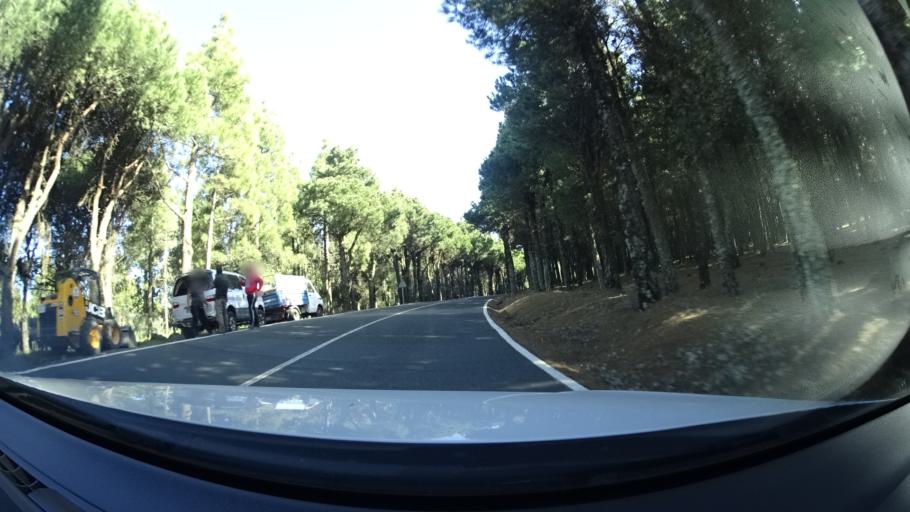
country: ES
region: Canary Islands
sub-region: Provincia de Las Palmas
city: Vega de San Mateo
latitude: 27.9658
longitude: -15.5470
